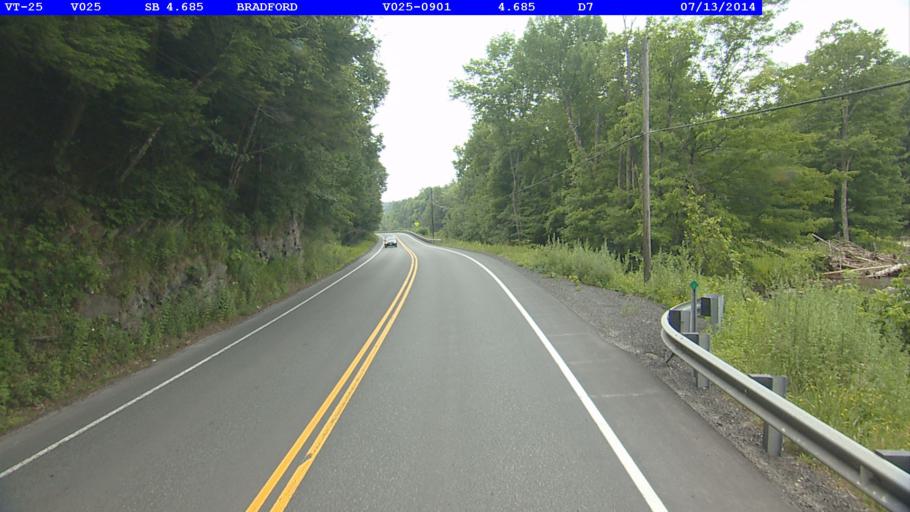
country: US
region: New Hampshire
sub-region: Grafton County
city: Haverhill
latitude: 44.0201
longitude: -72.1734
